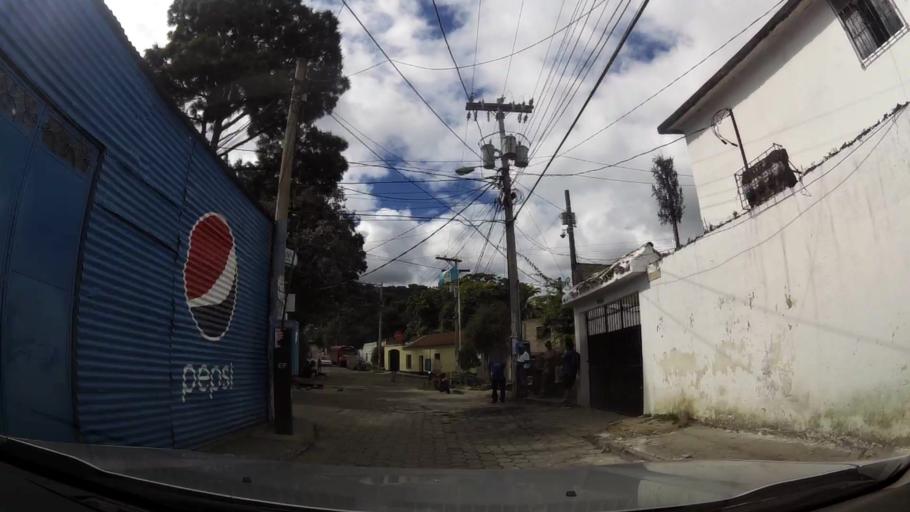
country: GT
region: Guatemala
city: Mixco
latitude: 14.6320
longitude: -90.6123
